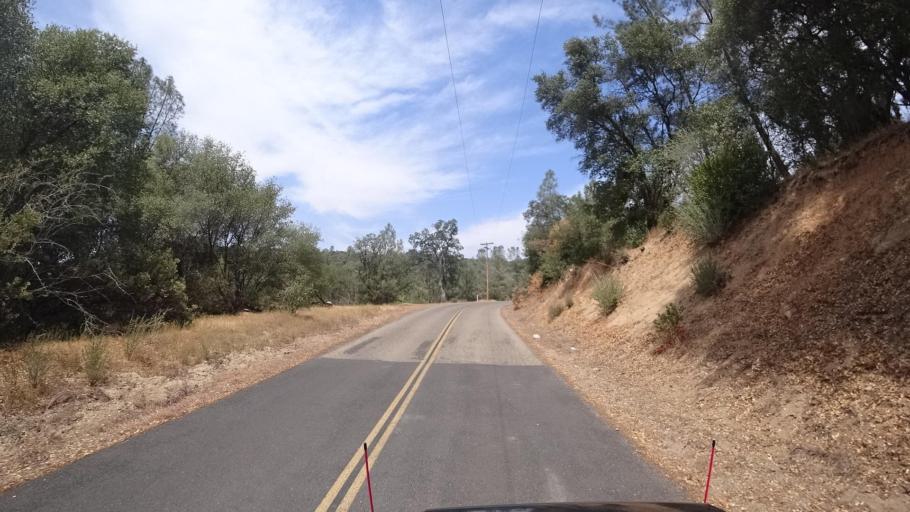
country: US
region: California
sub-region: Madera County
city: Ahwahnee
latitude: 37.4255
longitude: -119.8176
